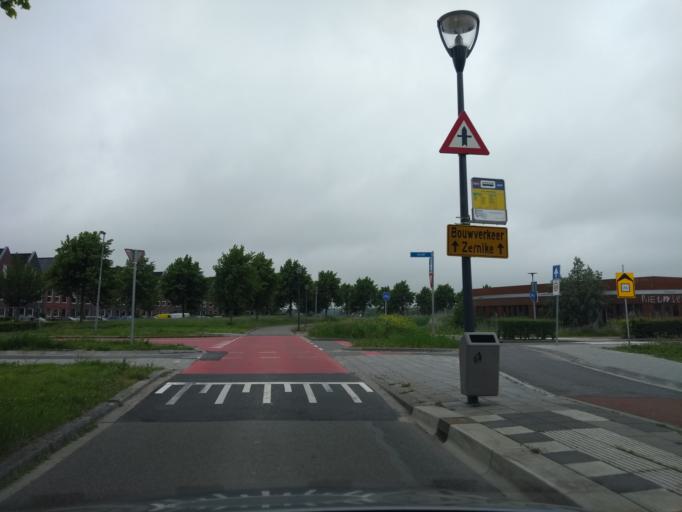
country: NL
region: Groningen
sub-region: Gemeente Groningen
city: Korrewegwijk
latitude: 53.2403
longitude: 6.5192
